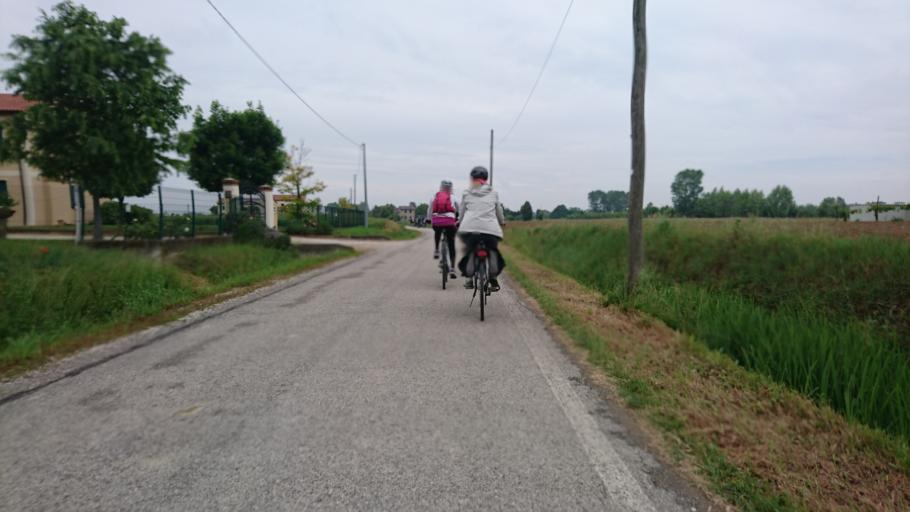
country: IT
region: Veneto
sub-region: Provincia di Padova
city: Montemerlo
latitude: 45.3916
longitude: 11.6916
